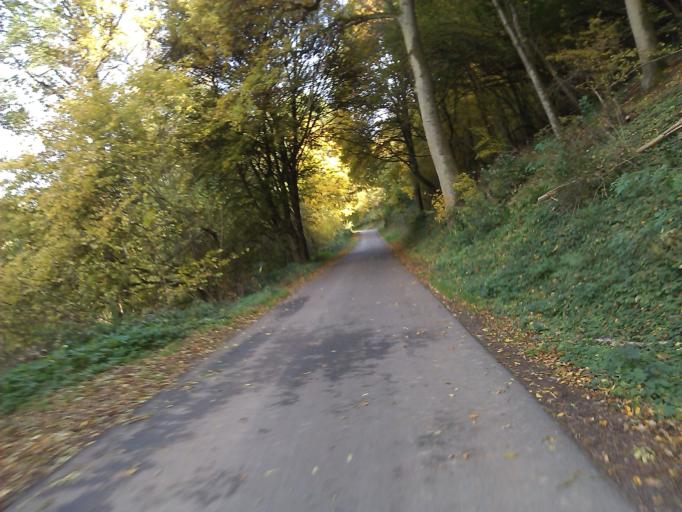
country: DE
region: Rheinland-Pfalz
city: Odenbach
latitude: 49.6776
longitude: 7.6461
